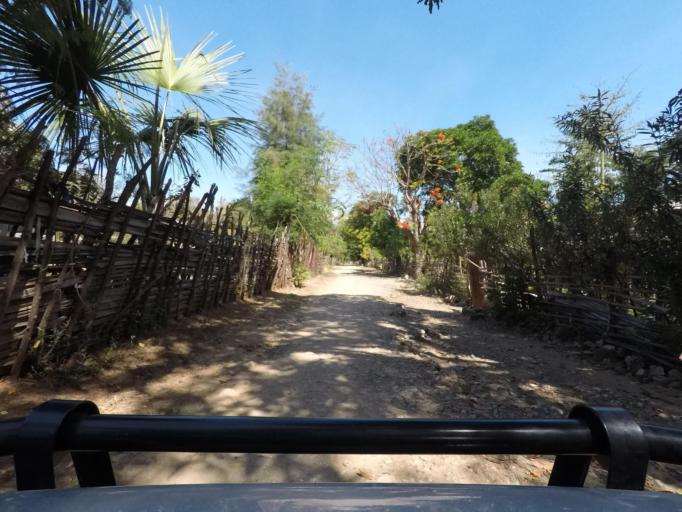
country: TL
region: Liquica
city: Maubara
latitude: -8.7846
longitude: 125.1035
